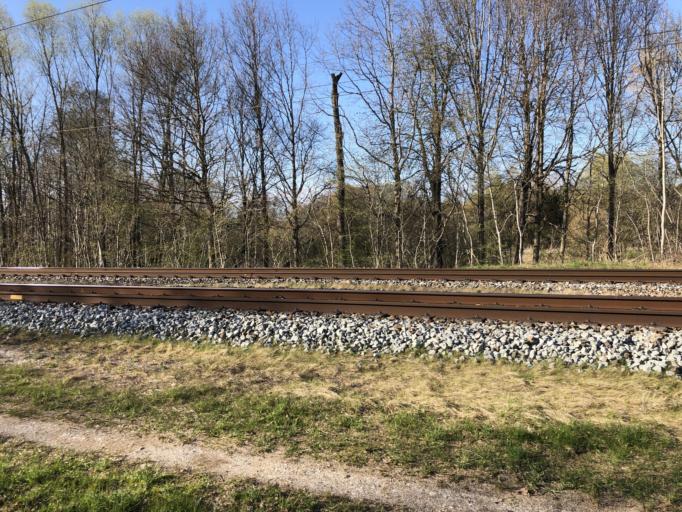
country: DK
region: South Denmark
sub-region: Nyborg Kommune
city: Nyborg
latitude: 55.3379
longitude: 10.7352
